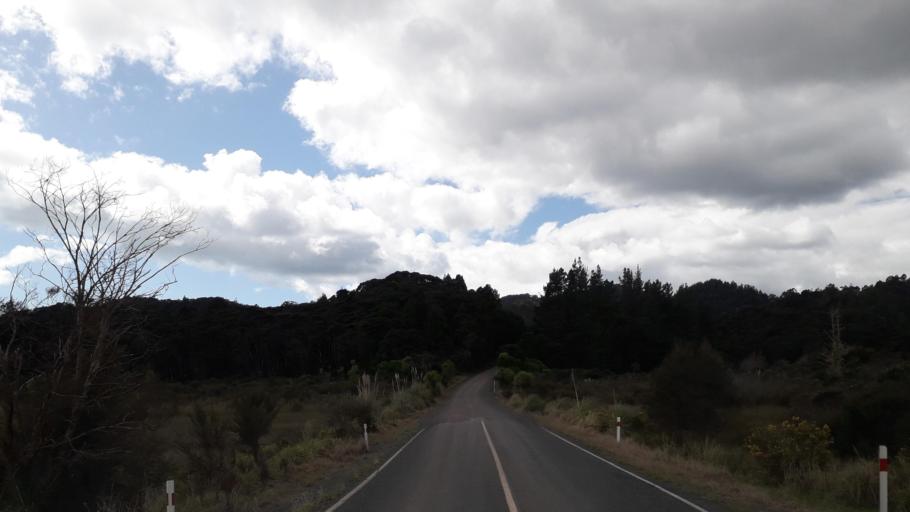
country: NZ
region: Northland
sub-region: Far North District
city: Paihia
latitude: -35.3263
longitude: 174.2328
